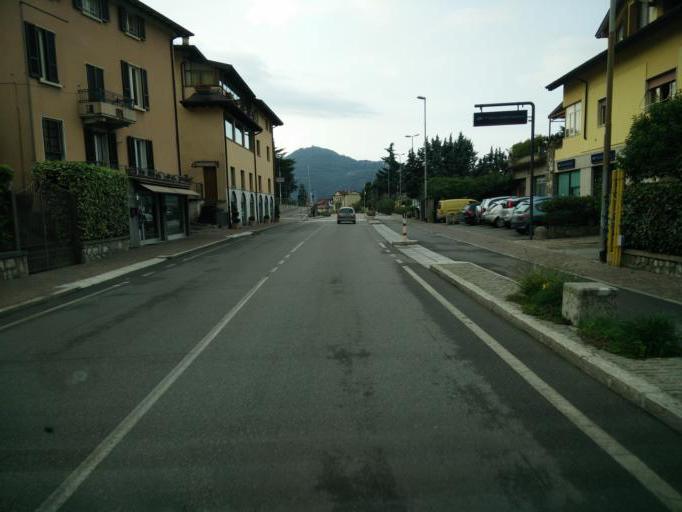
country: IT
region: Lombardy
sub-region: Provincia di Brescia
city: Marone
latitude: 45.7368
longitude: 10.0921
